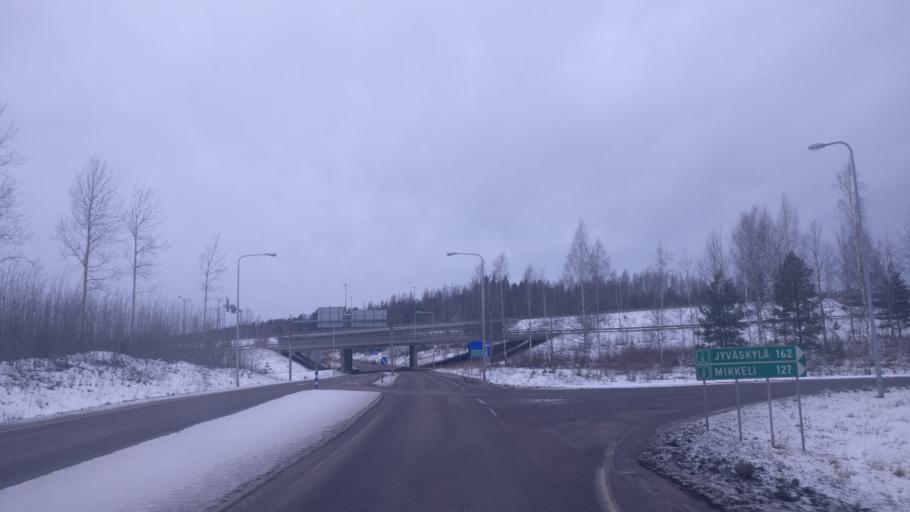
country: FI
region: Paijanne Tavastia
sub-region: Lahti
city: Lahti
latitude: 60.9680
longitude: 25.7189
